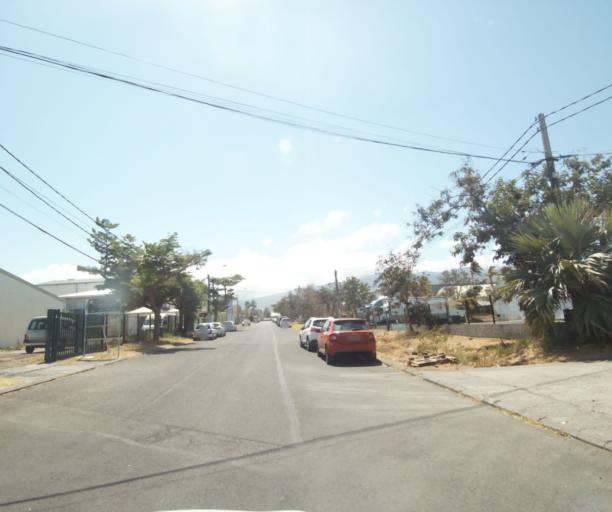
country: RE
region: Reunion
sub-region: Reunion
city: Le Port
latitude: -20.9630
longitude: 55.2958
